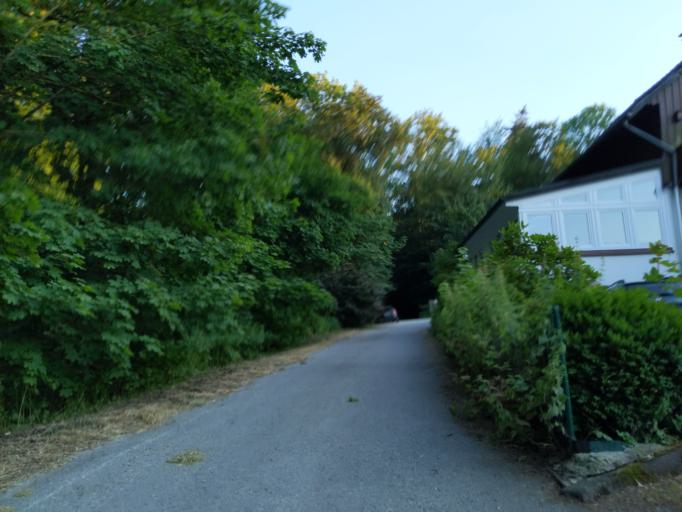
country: DE
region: North Rhine-Westphalia
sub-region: Regierungsbezirk Detmold
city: Bielefeld
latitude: 52.0209
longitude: 8.4899
